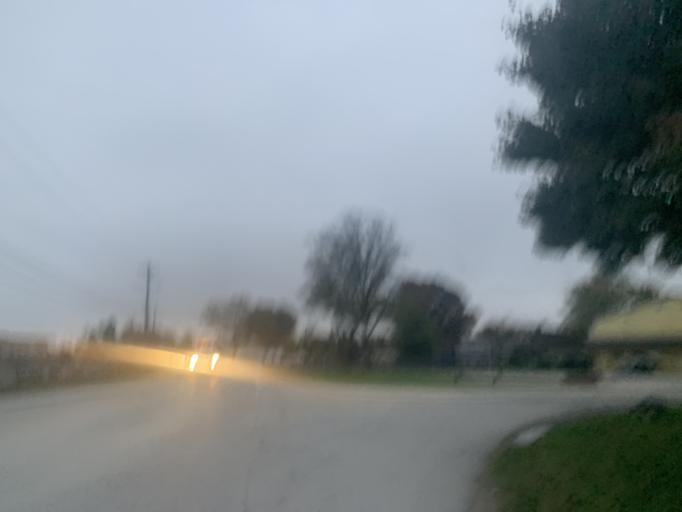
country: US
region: Kentucky
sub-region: Jefferson County
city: Shively
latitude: 38.2159
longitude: -85.8079
